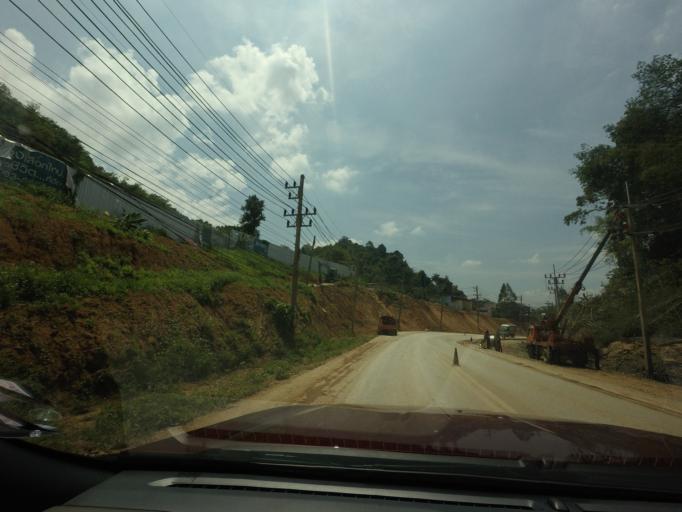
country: TH
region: Yala
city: Betong
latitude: 5.8039
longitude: 101.0693
